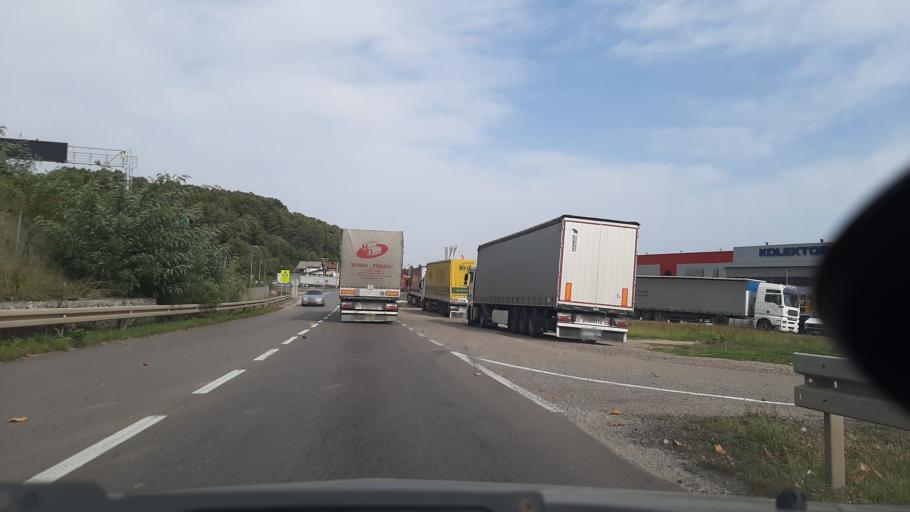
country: BA
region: Republika Srpska
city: Laktasi
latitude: 44.8759
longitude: 17.2822
